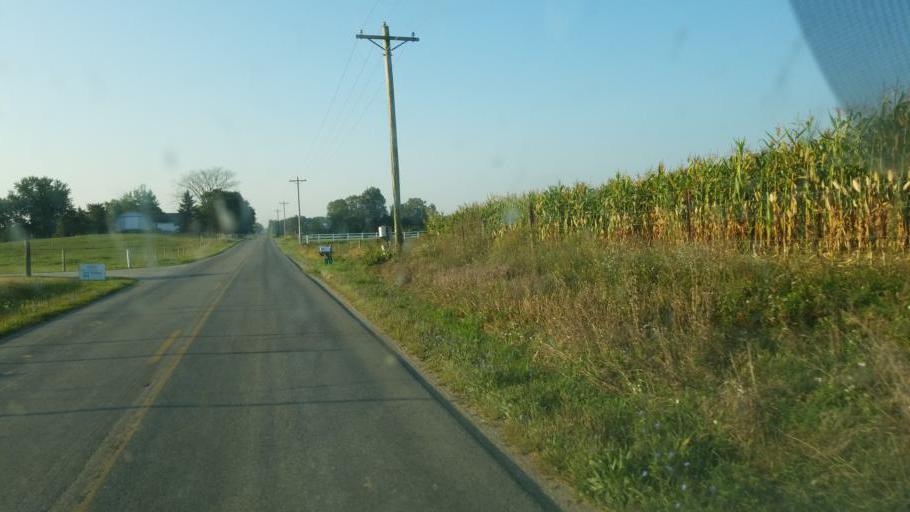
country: US
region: Indiana
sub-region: LaGrange County
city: Lagrange
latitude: 41.6190
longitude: -85.4245
